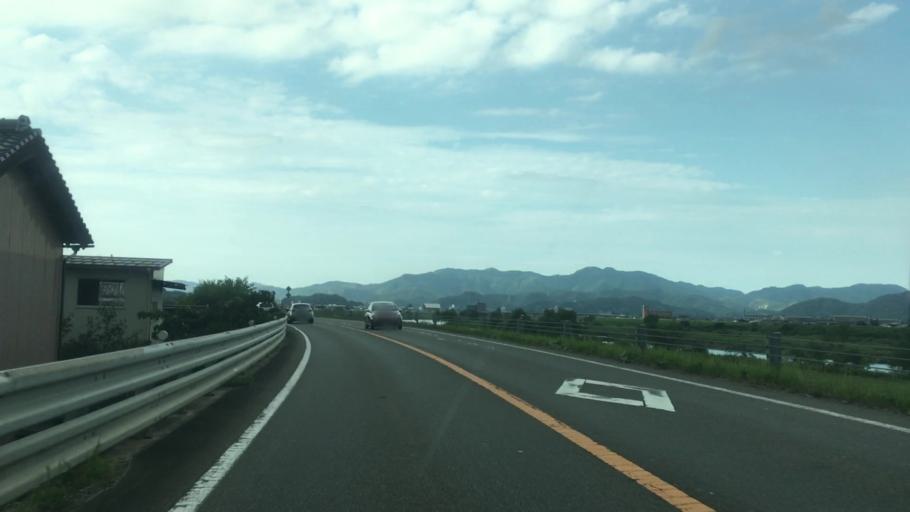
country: JP
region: Hyogo
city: Toyooka
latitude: 35.5122
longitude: 134.8217
